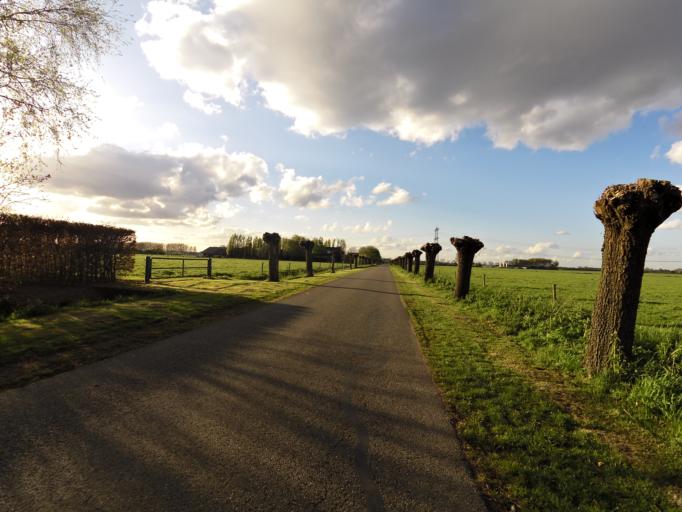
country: NL
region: Gelderland
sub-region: Gemeente Doesburg
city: Doesburg
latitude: 51.9641
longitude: 6.1204
